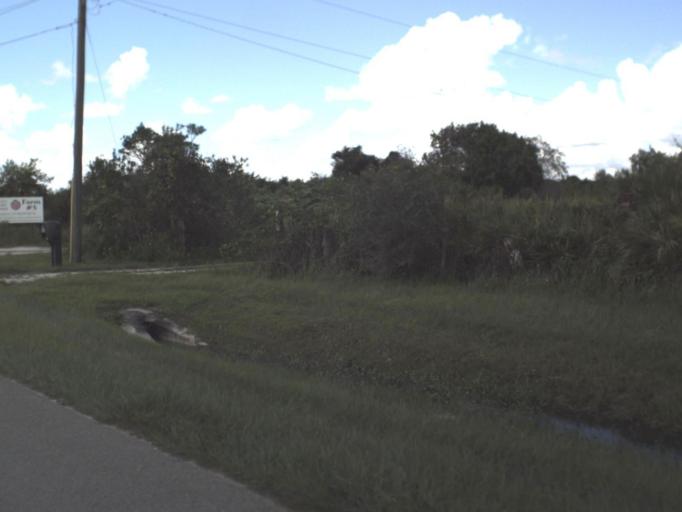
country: US
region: Florida
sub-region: Sarasota County
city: Lake Sarasota
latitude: 27.3632
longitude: -82.2022
